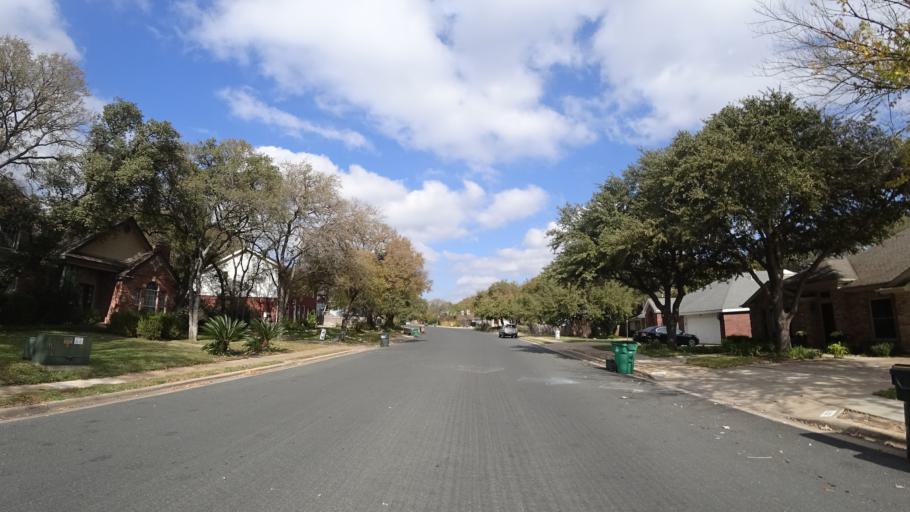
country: US
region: Texas
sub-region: Travis County
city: Shady Hollow
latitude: 30.1626
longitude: -97.8520
